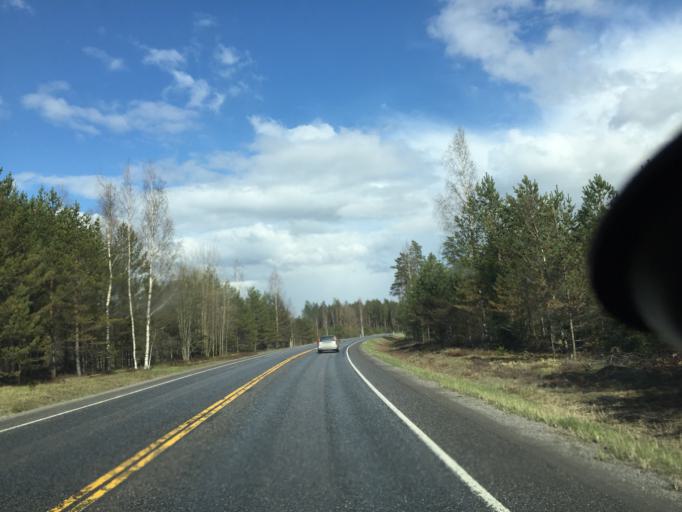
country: FI
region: Uusimaa
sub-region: Helsinki
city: Karjalohja
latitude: 60.1274
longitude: 23.8219
